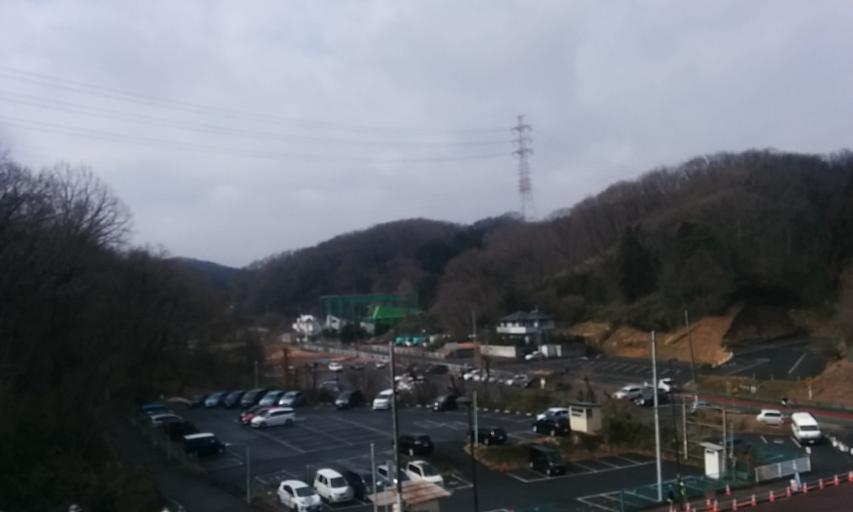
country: JP
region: Tokyo
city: Hino
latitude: 35.6467
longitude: 139.4035
